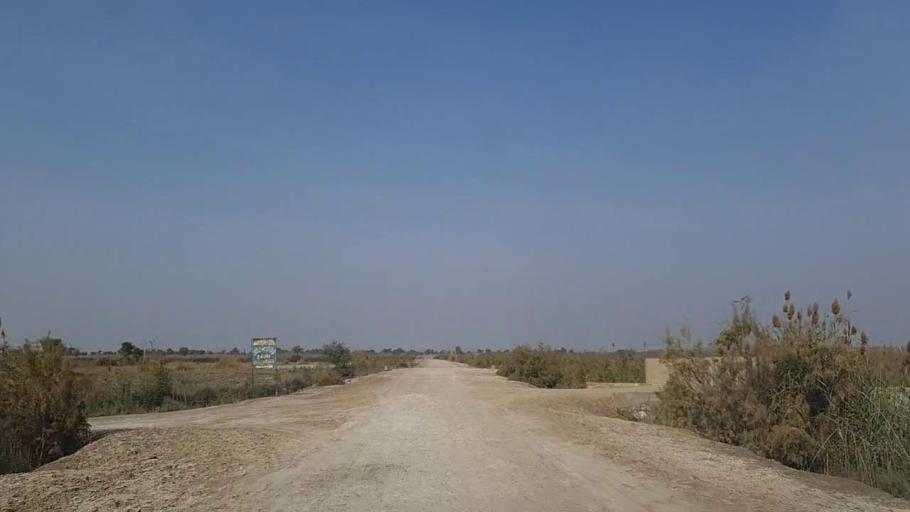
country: PK
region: Sindh
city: Daur
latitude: 26.5040
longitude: 68.4796
